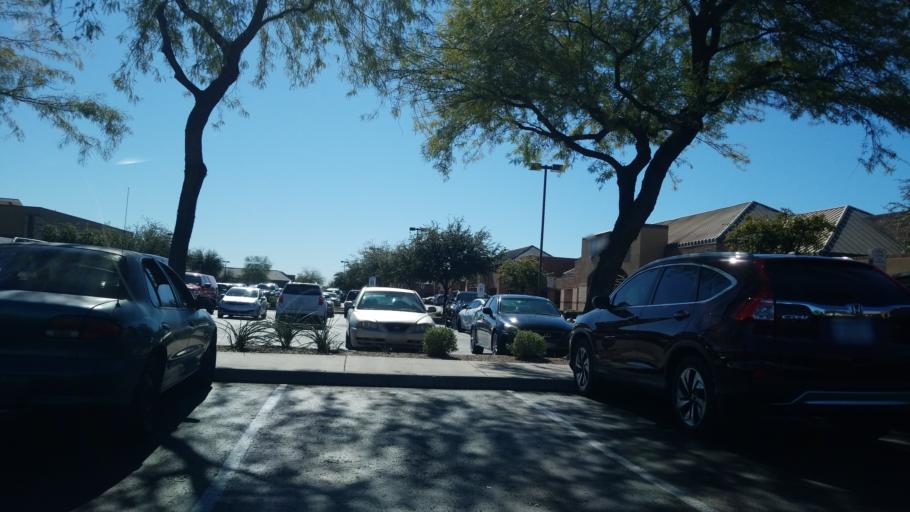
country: US
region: Arizona
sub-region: Maricopa County
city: Paradise Valley
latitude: 33.6174
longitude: -111.9269
